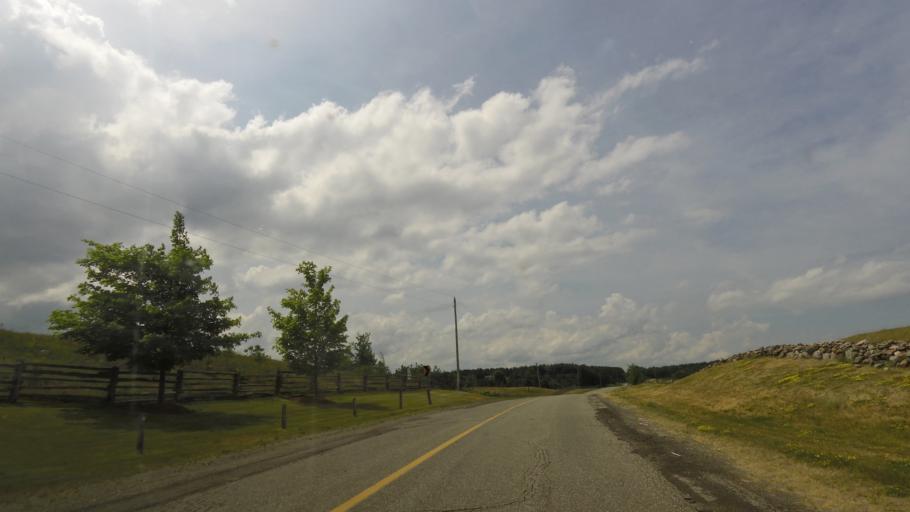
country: CA
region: Ontario
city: Orangeville
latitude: 43.8756
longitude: -79.9209
